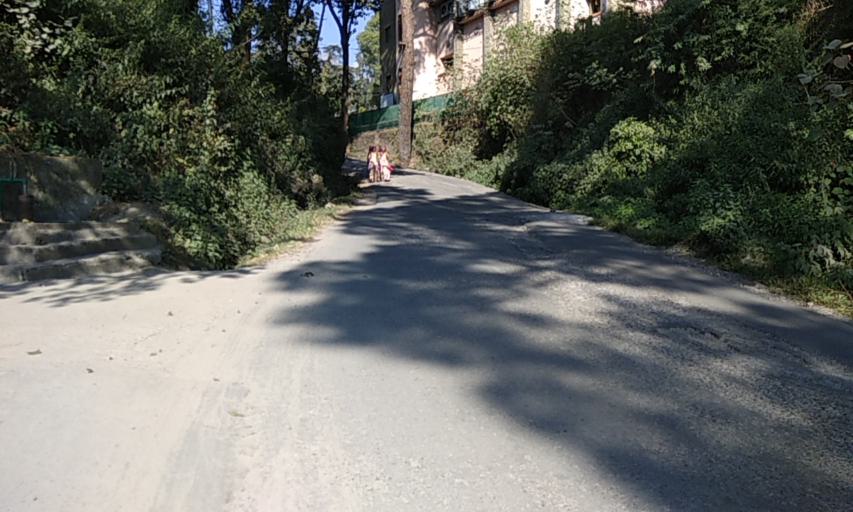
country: IN
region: Himachal Pradesh
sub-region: Kangra
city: Palampur
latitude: 32.1108
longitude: 76.5349
